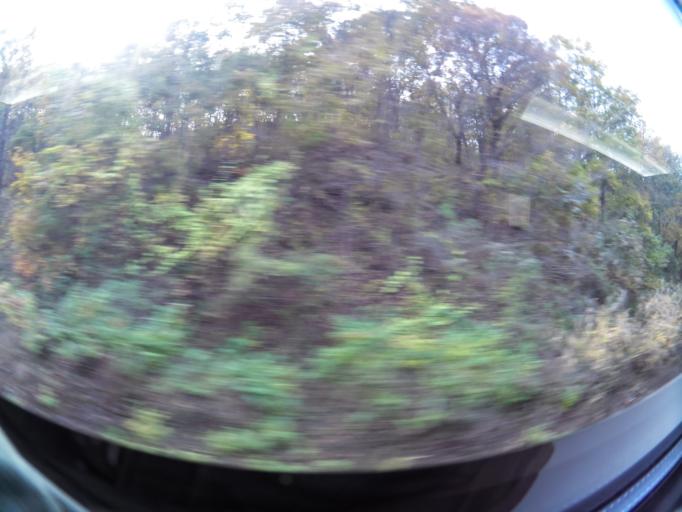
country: KR
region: Gyeongsangbuk-do
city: Gimcheon
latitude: 36.1337
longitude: 128.0203
